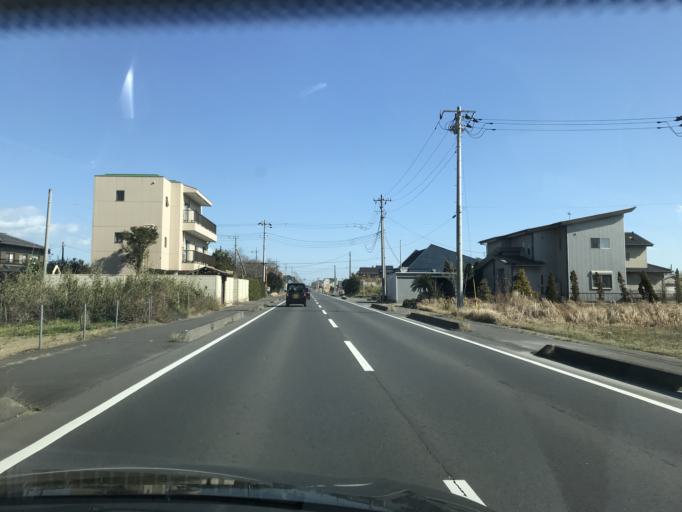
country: JP
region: Chiba
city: Omigawa
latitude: 35.8683
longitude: 140.6598
